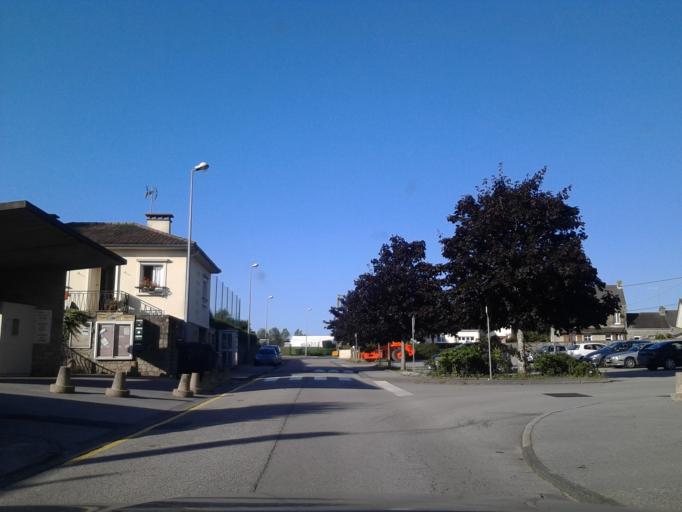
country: FR
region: Lower Normandy
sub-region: Departement de la Manche
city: Valognes
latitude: 49.5133
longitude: -1.4715
